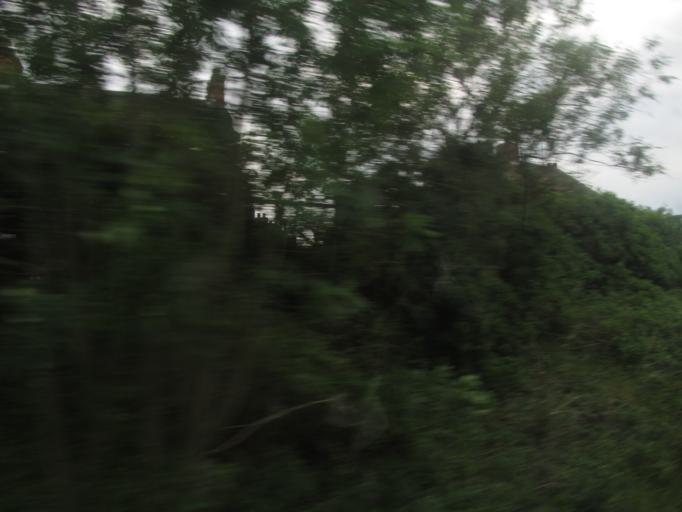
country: GB
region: England
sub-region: Northamptonshire
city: Desborough
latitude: 52.4445
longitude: -0.8176
